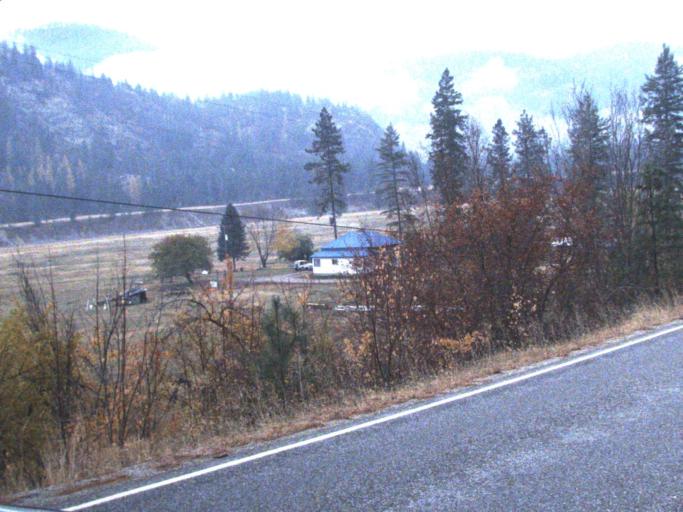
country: CA
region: British Columbia
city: Grand Forks
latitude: 48.9780
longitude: -118.2240
